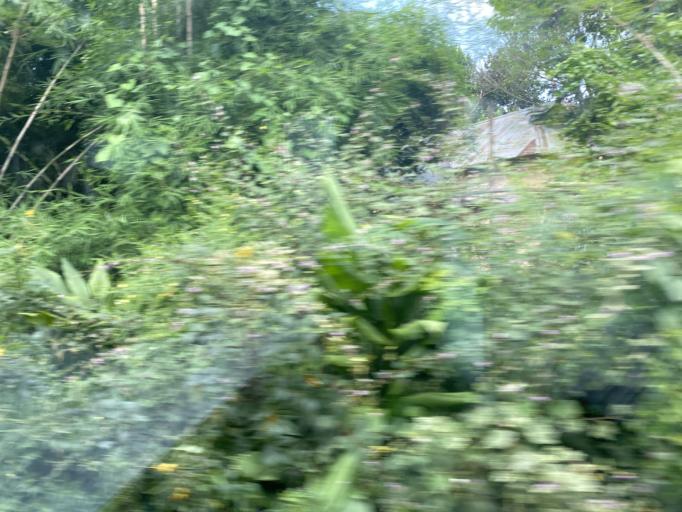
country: IN
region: Tripura
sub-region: West Tripura
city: Agartala
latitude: 23.9990
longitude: 91.2916
